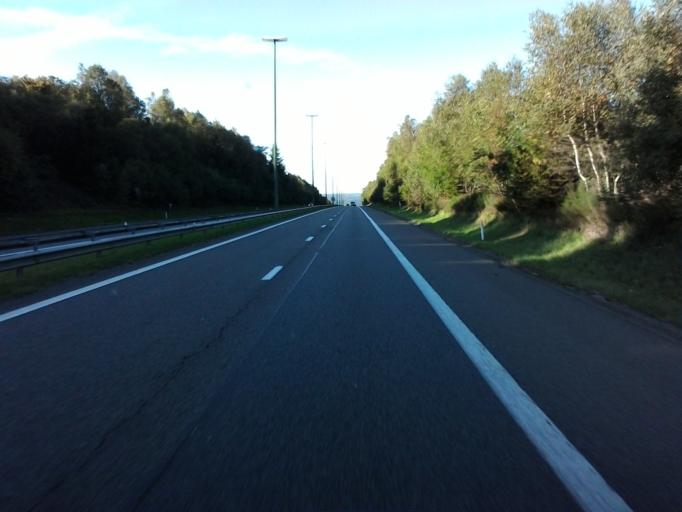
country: BE
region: Wallonia
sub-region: Province du Luxembourg
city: Houffalize
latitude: 50.1071
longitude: 5.7588
